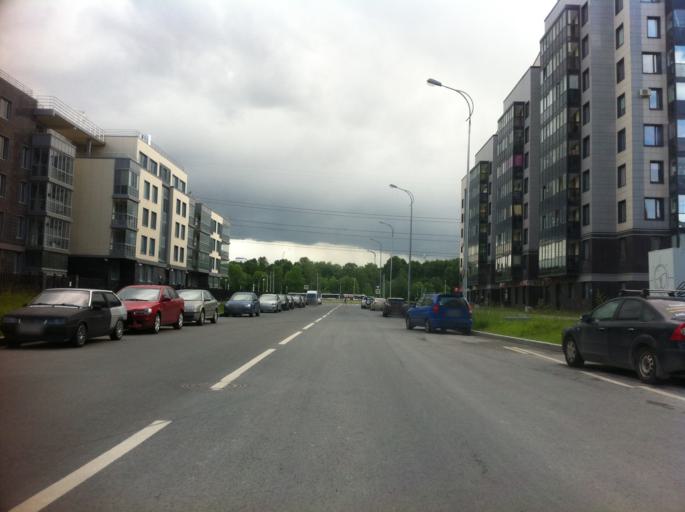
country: RU
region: St.-Petersburg
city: Sosnovaya Polyana
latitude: 59.8495
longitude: 30.1558
